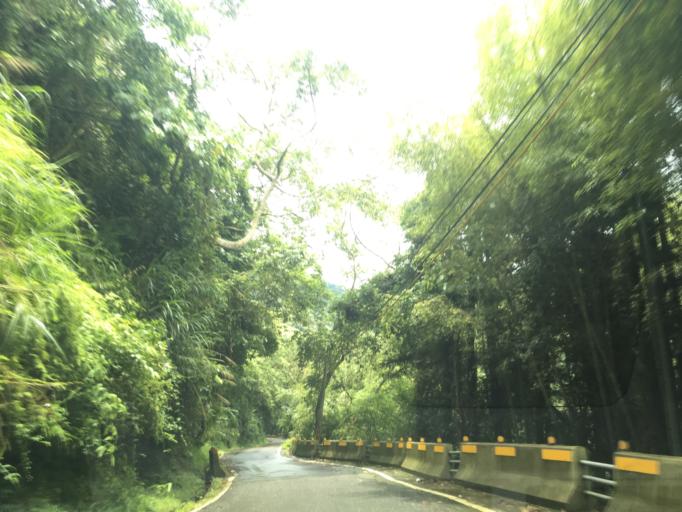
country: TW
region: Taiwan
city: Lugu
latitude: 23.5509
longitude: 120.6796
